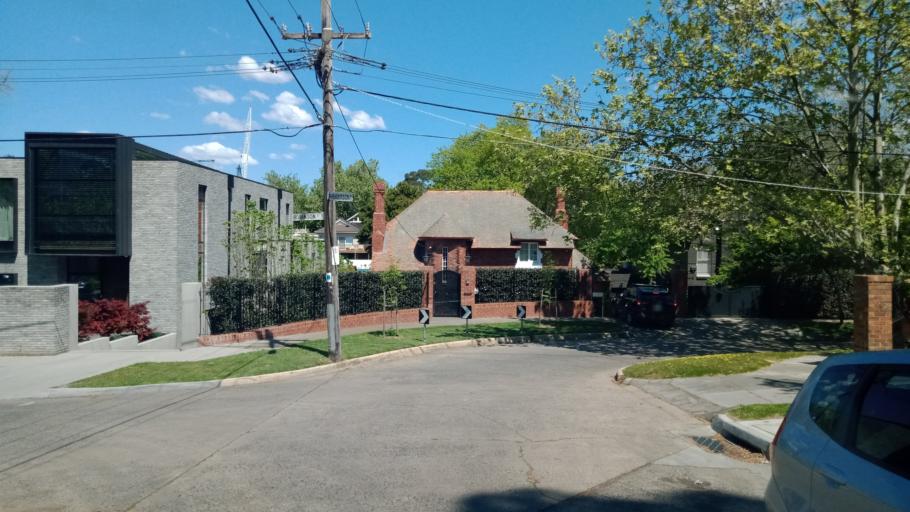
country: AU
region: Victoria
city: Toorak
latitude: -37.8485
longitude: 145.0346
